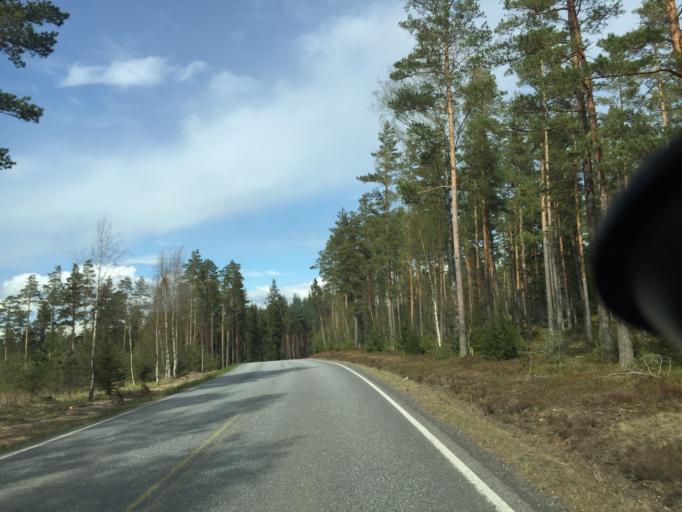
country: FI
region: Varsinais-Suomi
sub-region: Salo
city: Pernioe
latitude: 60.0297
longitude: 23.1828
